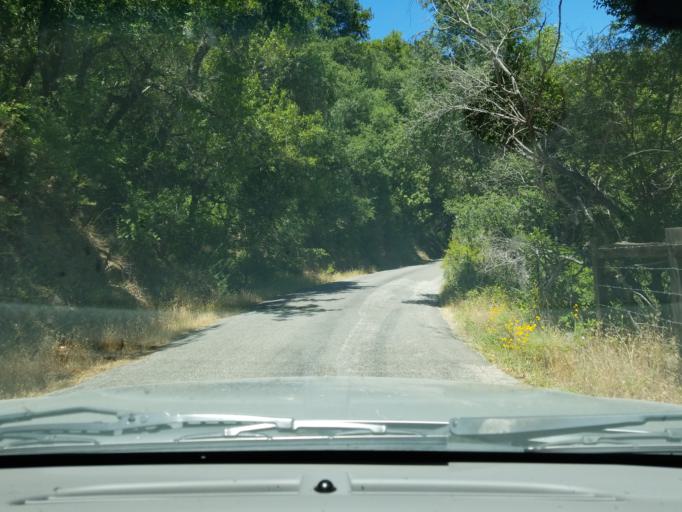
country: US
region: California
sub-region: Monterey County
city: Gonzales
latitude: 36.3556
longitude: -121.5478
